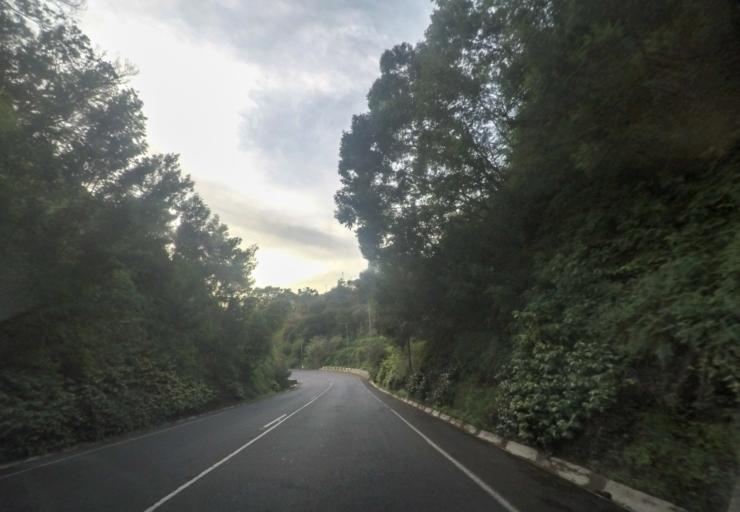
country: PT
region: Madeira
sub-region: Funchal
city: Nossa Senhora do Monte
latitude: 32.6565
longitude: -16.8804
